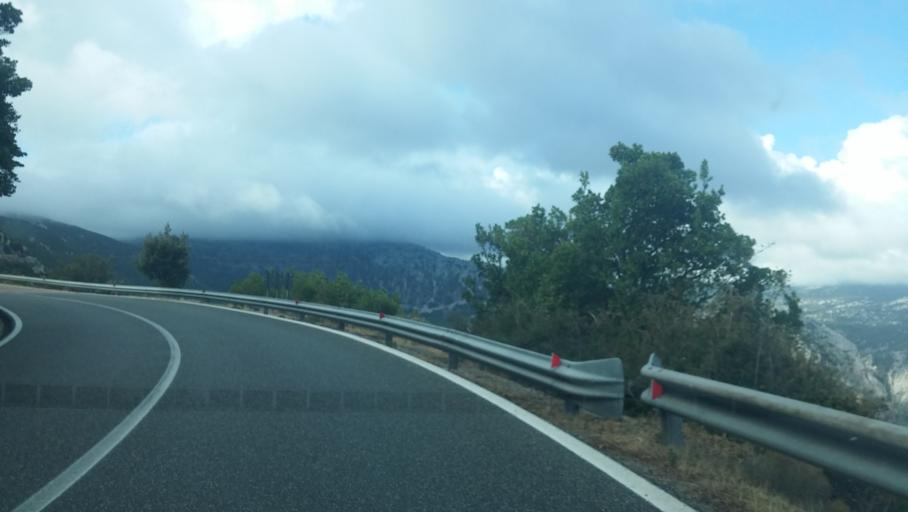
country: IT
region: Sardinia
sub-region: Provincia di Ogliastra
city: Urzulei
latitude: 40.1844
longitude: 9.5338
